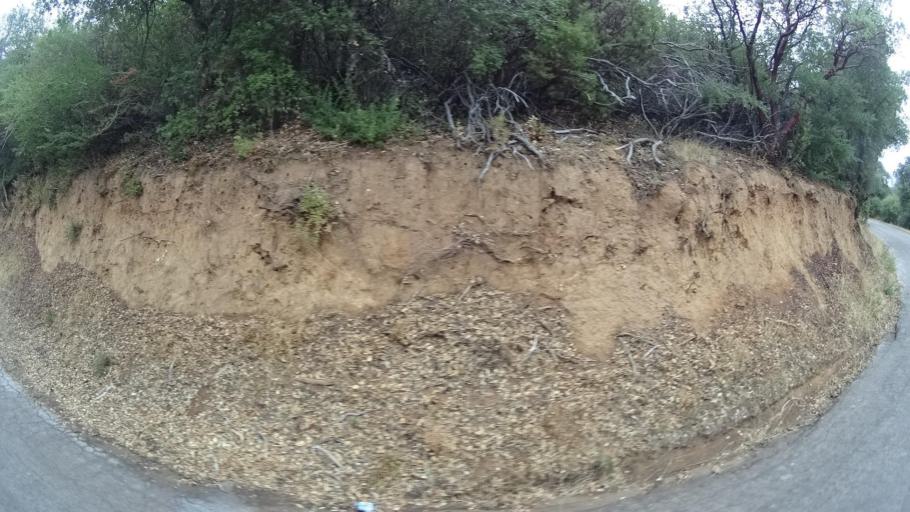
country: US
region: California
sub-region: San Diego County
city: Julian
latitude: 33.0236
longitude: -116.6363
